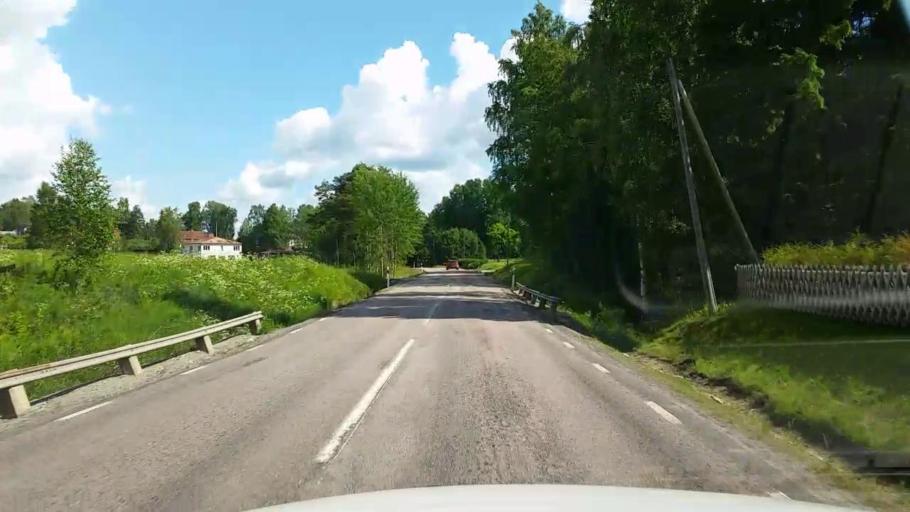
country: SE
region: Vaestmanland
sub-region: Kopings Kommun
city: Kolsva
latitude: 59.7030
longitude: 15.7902
